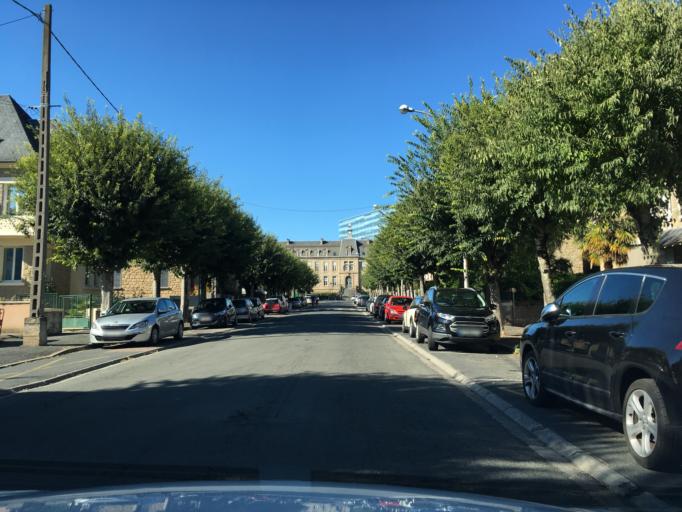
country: FR
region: Limousin
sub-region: Departement de la Correze
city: Brive-la-Gaillarde
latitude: 45.1665
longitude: 1.5333
